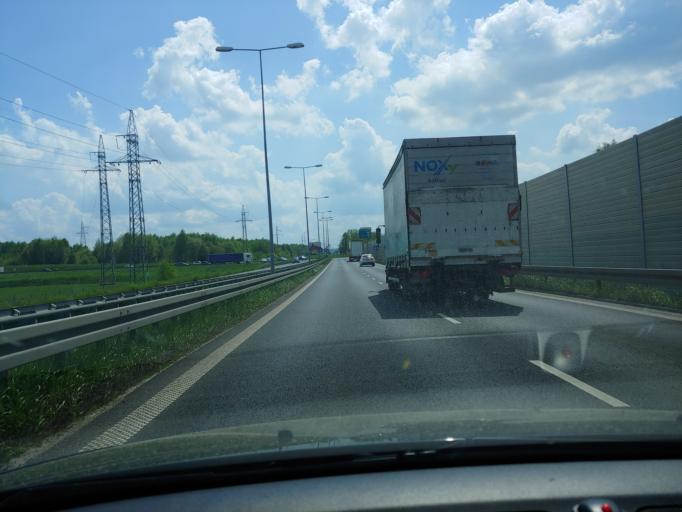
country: PL
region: Lesser Poland Voivodeship
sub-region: Powiat tarnowski
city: Tarnow
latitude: 50.0509
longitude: 21.0110
